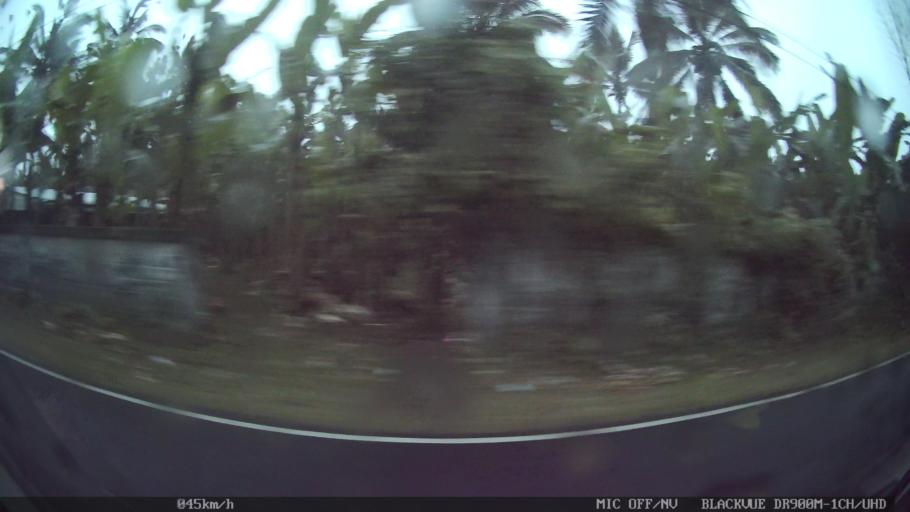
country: ID
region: Bali
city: Banjar Taro Kelod
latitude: -8.3709
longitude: 115.2693
